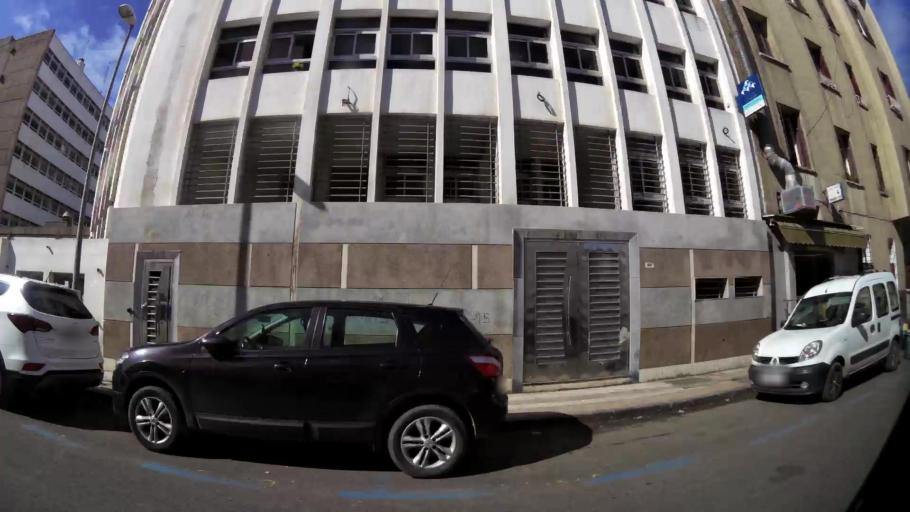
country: MA
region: Grand Casablanca
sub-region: Casablanca
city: Casablanca
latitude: 33.5925
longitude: -7.5940
